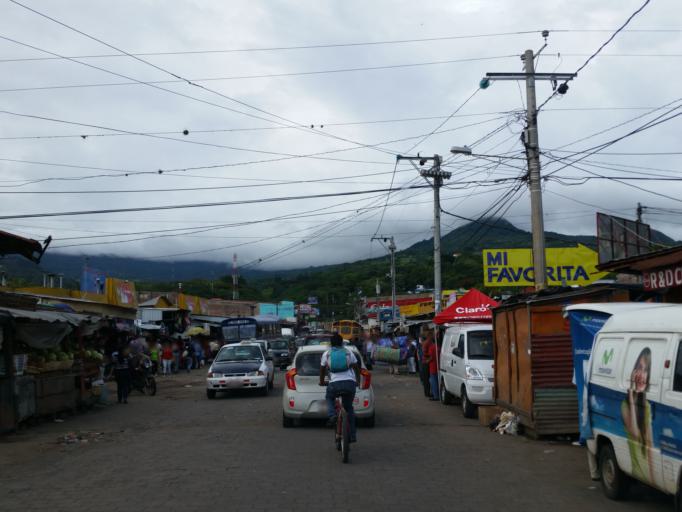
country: NI
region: Matagalpa
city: Matagalpa
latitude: 12.9340
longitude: -85.9121
